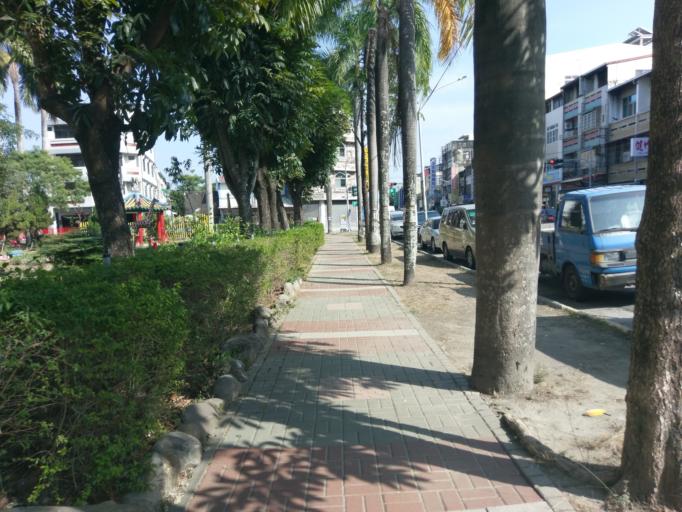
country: TW
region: Taiwan
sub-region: Yunlin
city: Douliu
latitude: 23.7118
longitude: 120.5526
